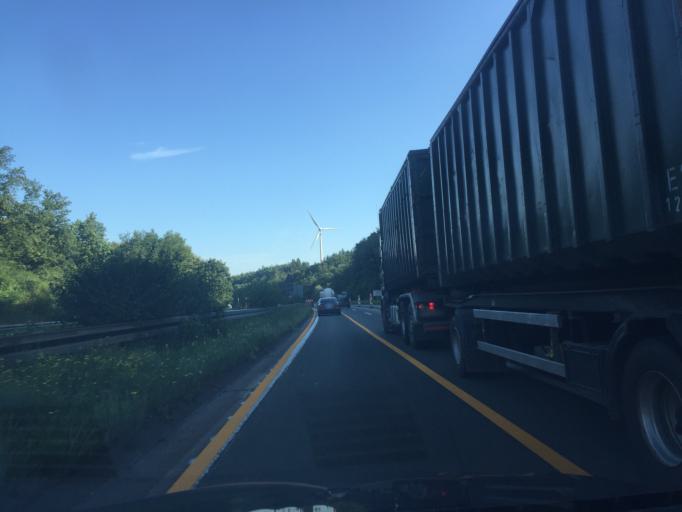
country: DE
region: North Rhine-Westphalia
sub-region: Regierungsbezirk Arnsberg
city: Nachrodt-Wiblingwerde
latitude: 51.3091
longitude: 7.5554
